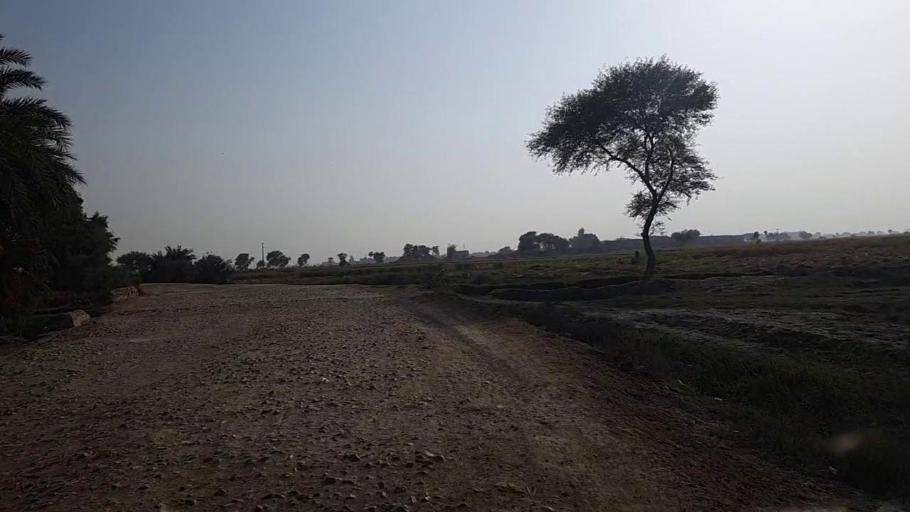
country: PK
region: Sindh
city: Kandhkot
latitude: 28.2869
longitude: 69.2581
